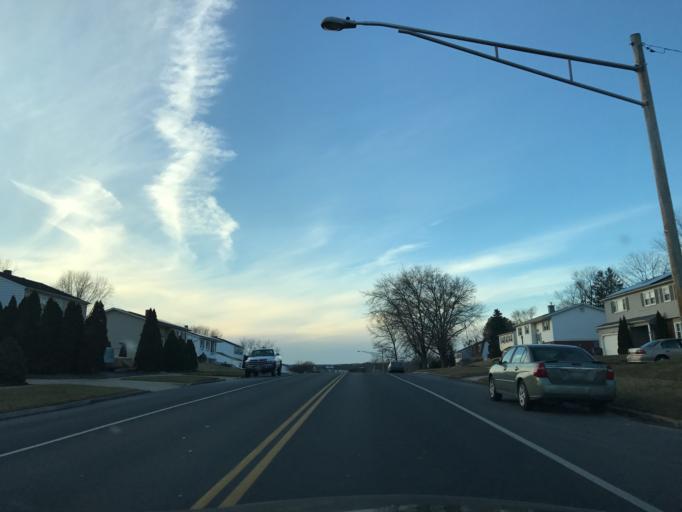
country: US
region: Maryland
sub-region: Harford County
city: Joppatowne
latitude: 39.4067
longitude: -76.3463
